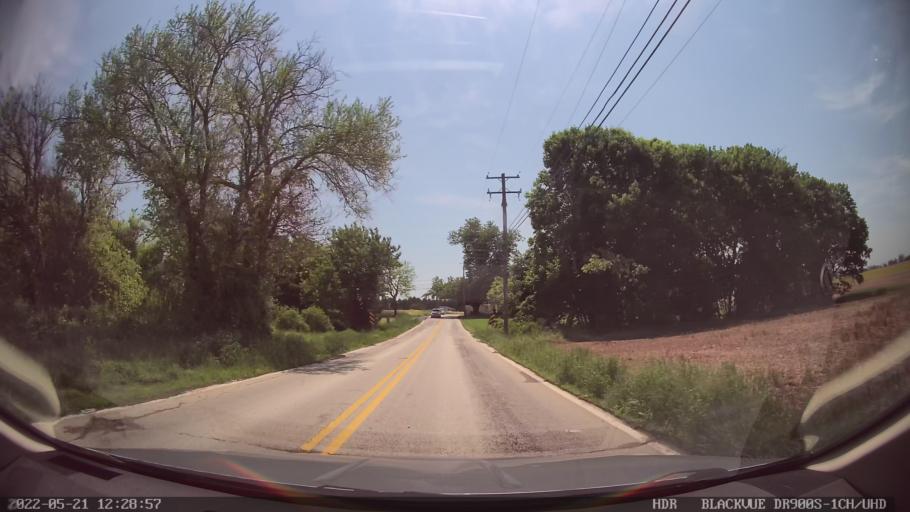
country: US
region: Pennsylvania
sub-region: Berks County
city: Bally
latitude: 40.3657
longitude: -75.5931
